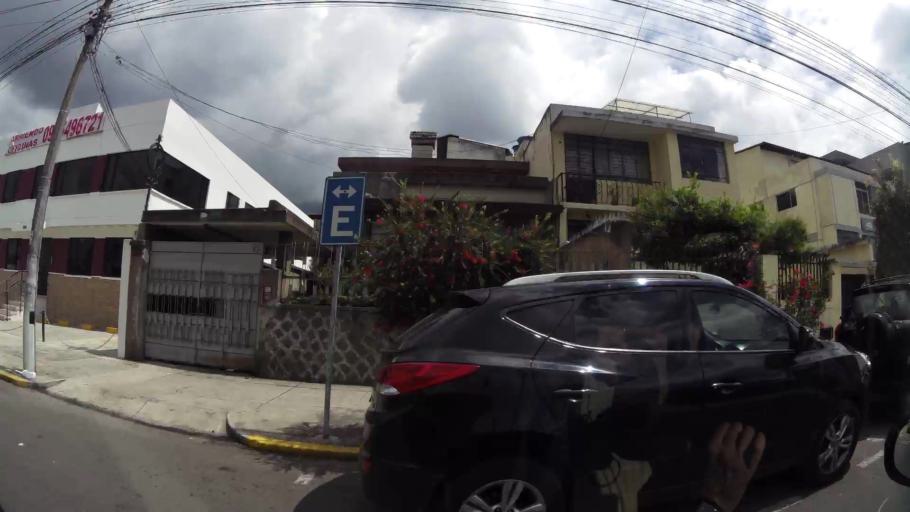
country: EC
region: Pichincha
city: Quito
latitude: -0.1888
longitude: -78.4949
